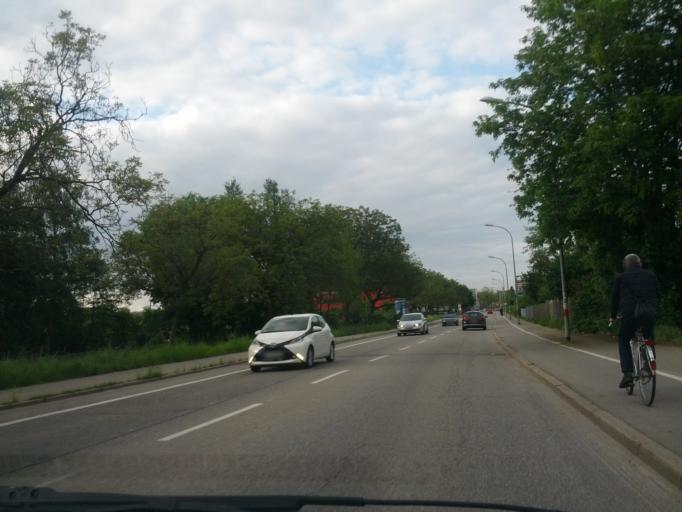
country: DE
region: Baden-Wuerttemberg
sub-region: Freiburg Region
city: Merzhausen
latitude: 47.9885
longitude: 7.8288
